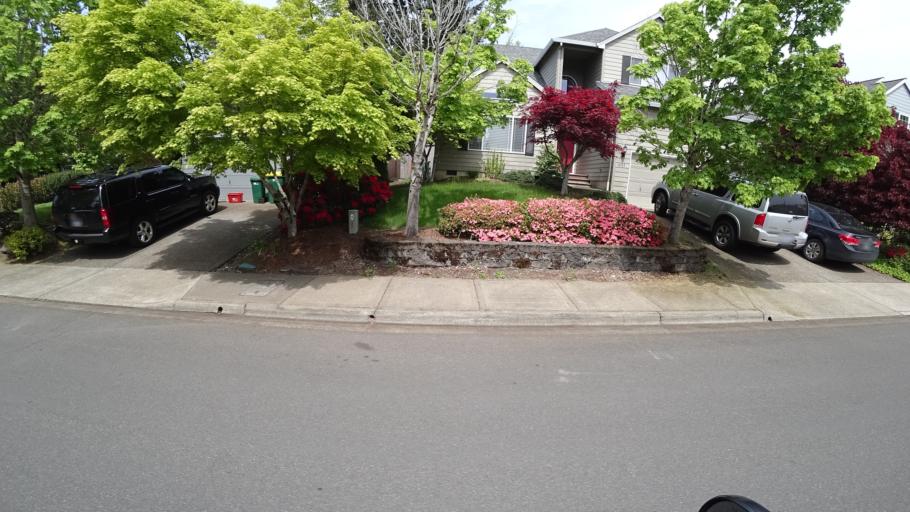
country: US
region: Oregon
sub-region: Washington County
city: Aloha
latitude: 45.4628
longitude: -122.8501
